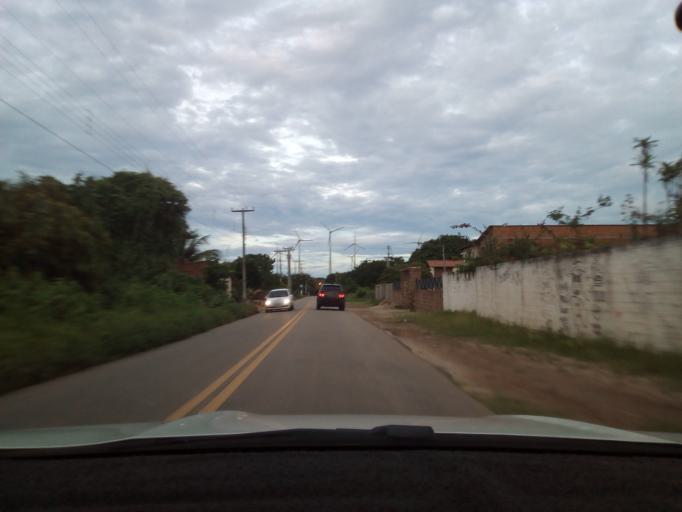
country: BR
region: Ceara
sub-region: Beberibe
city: Beberibe
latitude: -4.1843
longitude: -38.0969
